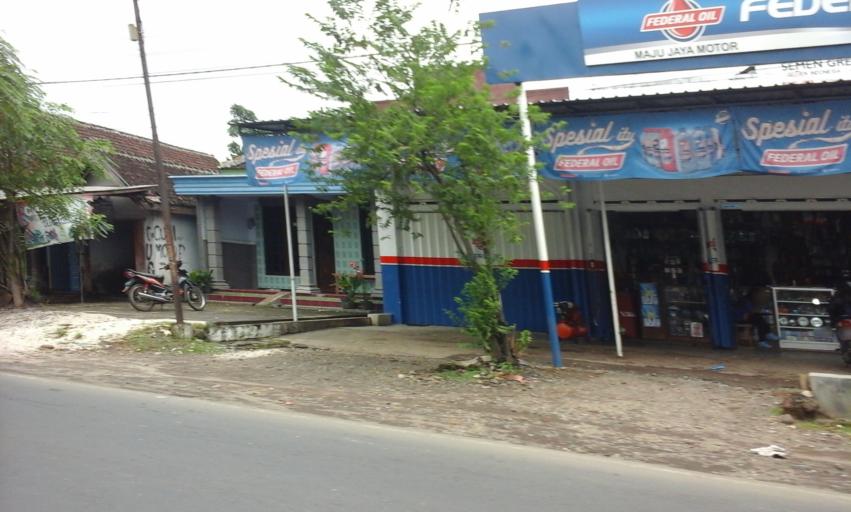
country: ID
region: East Java
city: Klatakan
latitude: -8.1921
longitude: 113.5014
